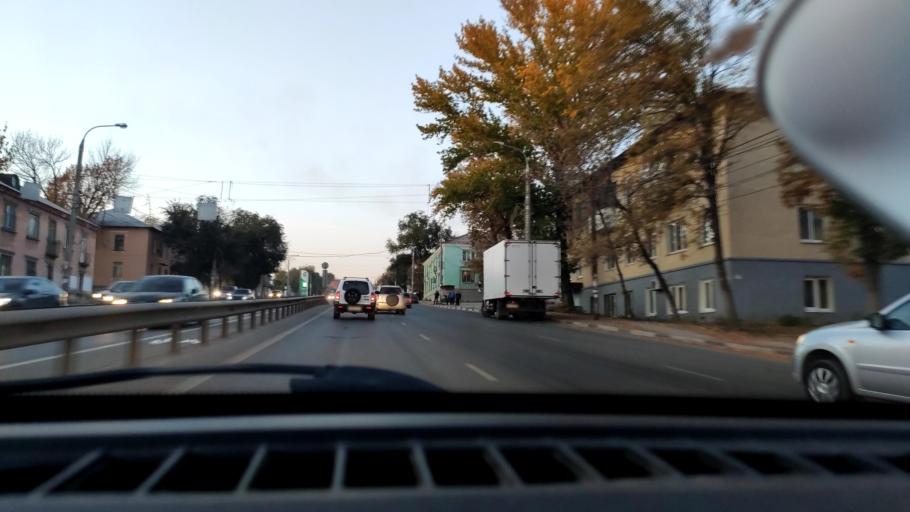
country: RU
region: Samara
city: Samara
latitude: 53.1798
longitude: 50.1919
